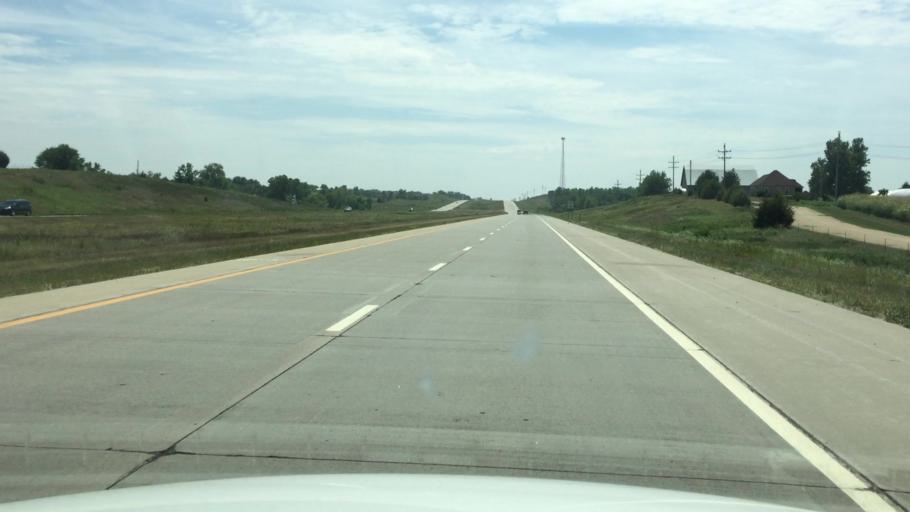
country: US
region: Kansas
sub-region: Jackson County
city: Holton
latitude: 39.2591
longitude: -95.7201
